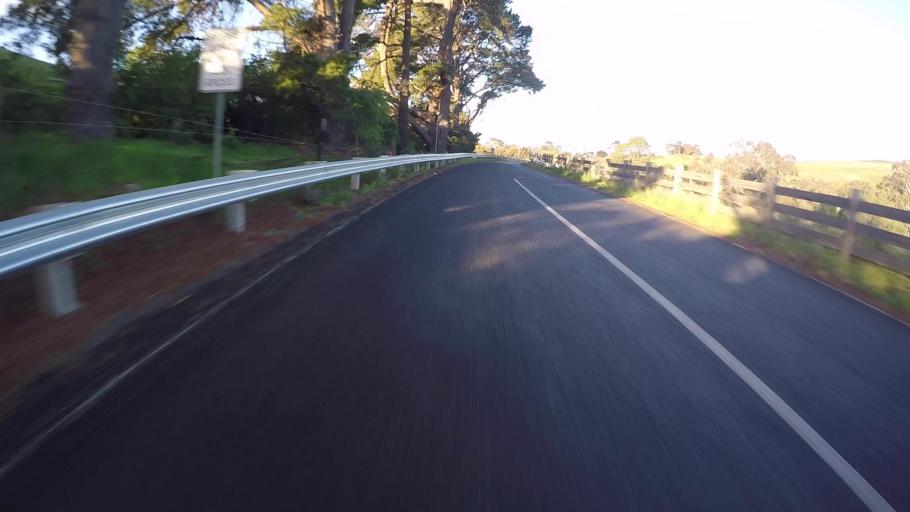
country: AU
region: Victoria
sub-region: Greater Geelong
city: Wandana Heights
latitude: -38.1452
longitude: 144.1858
